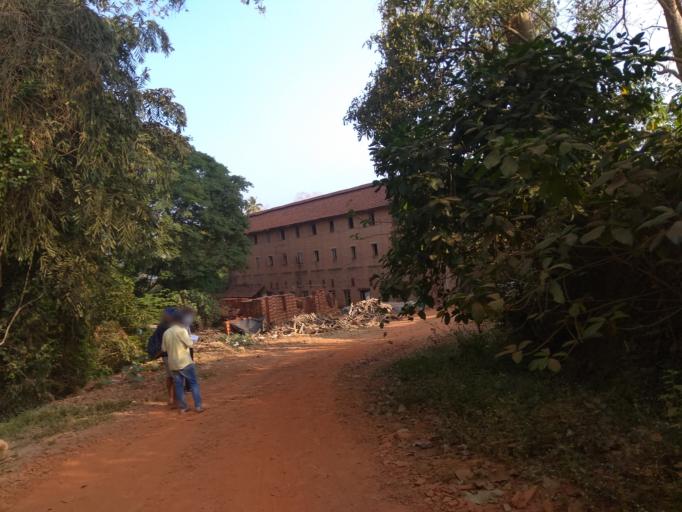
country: IN
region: Karnataka
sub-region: Dakshina Kannada
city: Ullal
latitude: 12.8447
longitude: 74.8539
